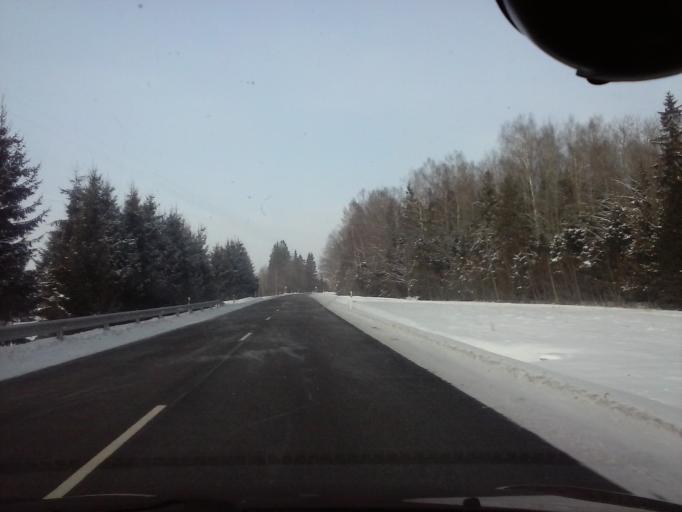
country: EE
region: Viljandimaa
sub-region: Abja vald
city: Abja-Paluoja
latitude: 58.3051
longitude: 25.2993
